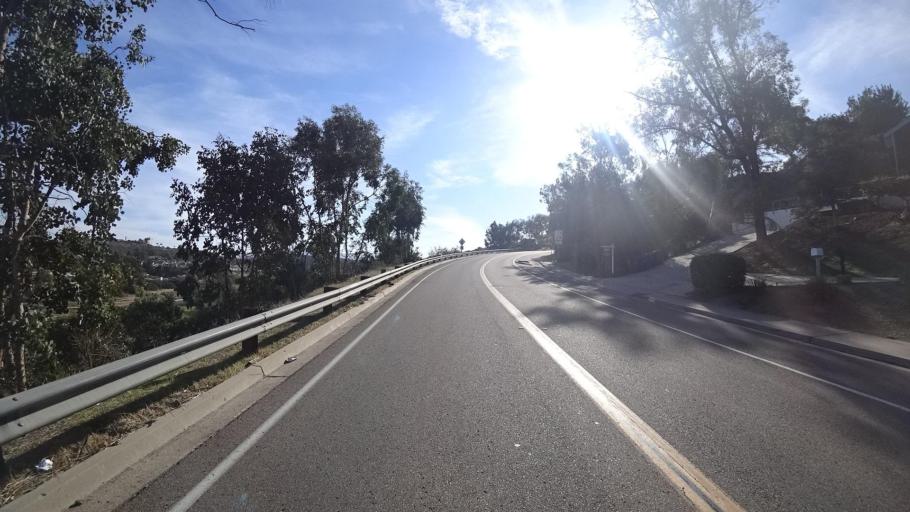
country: US
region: California
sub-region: San Diego County
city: Casa de Oro-Mount Helix
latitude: 32.7446
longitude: -116.9617
